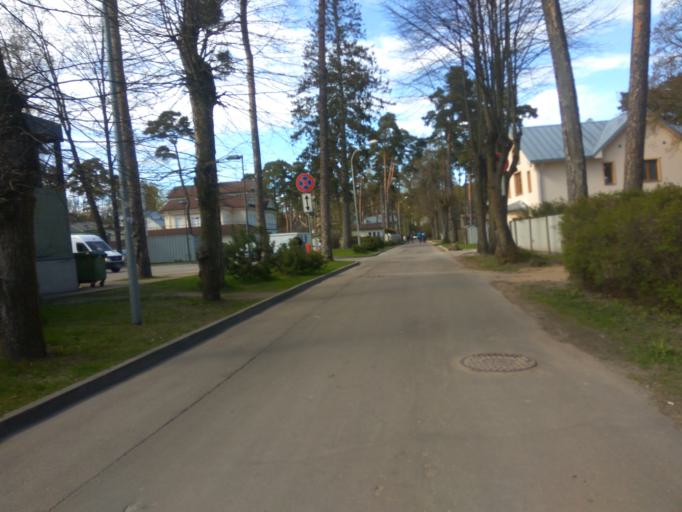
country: LV
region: Jurmala
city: Jurmala
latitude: 56.9740
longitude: 23.8041
